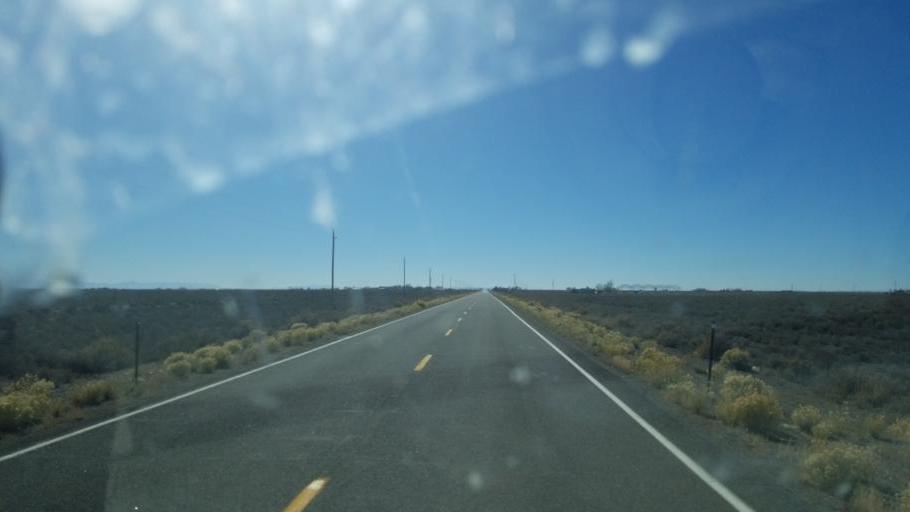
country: US
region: Colorado
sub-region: Saguache County
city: Center
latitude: 37.7699
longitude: -105.8833
